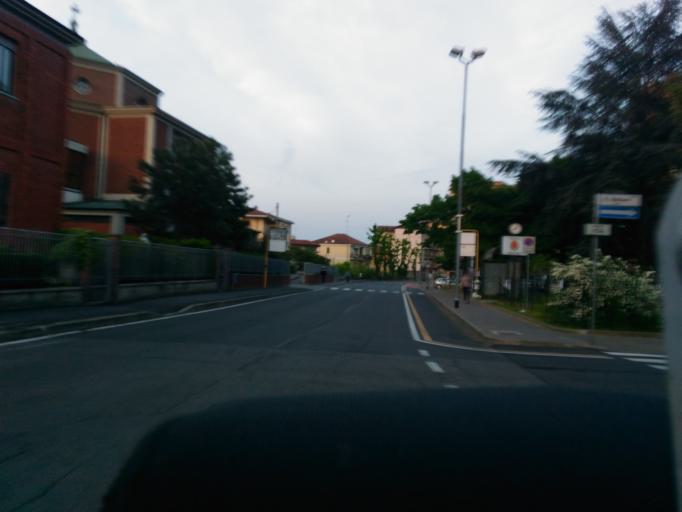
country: IT
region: Lombardy
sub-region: Provincia di Lodi
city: Lodi
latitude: 45.3116
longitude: 9.4895
